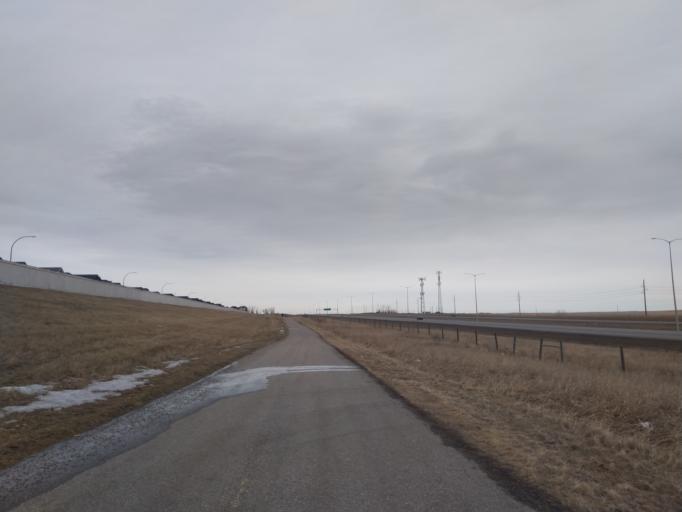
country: CA
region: Alberta
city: Chestermere
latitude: 51.1191
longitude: -113.9226
